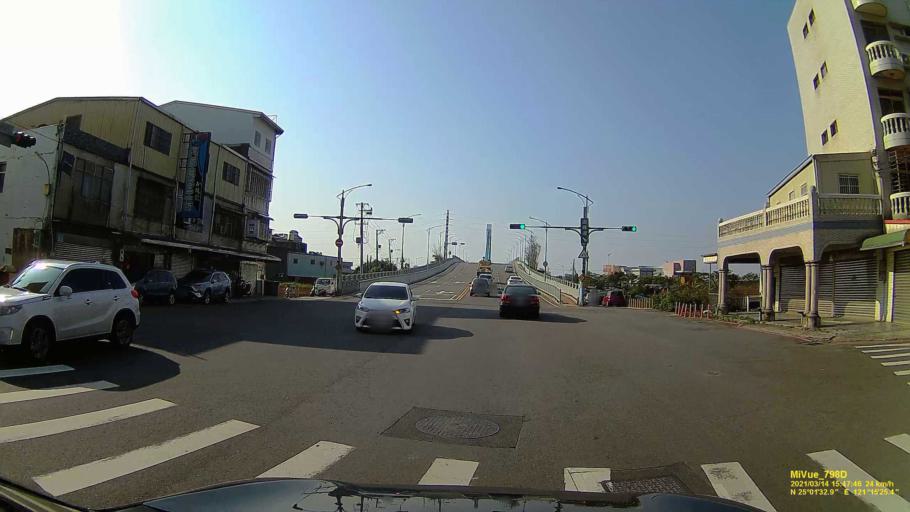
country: TW
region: Taiwan
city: Taoyuan City
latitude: 25.0261
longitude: 121.2568
